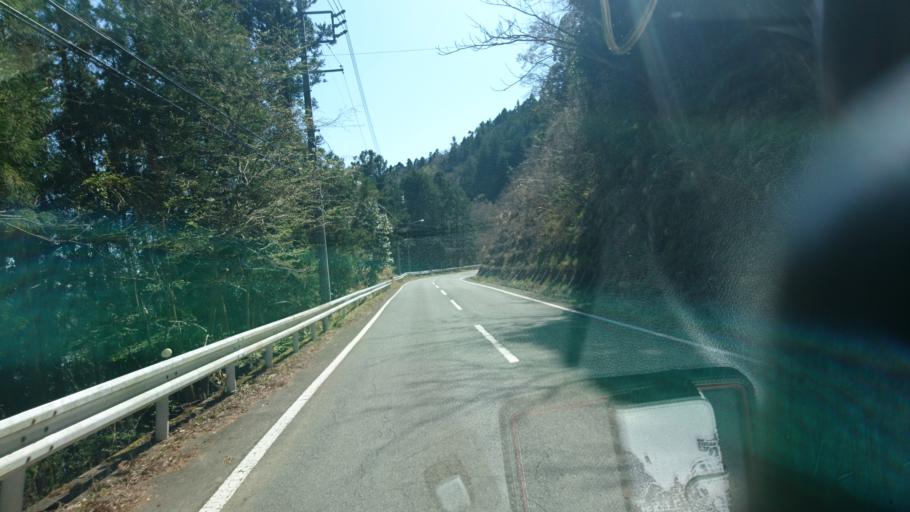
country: JP
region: Shizuoka
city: Fujinomiya
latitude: 35.3527
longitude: 138.4377
